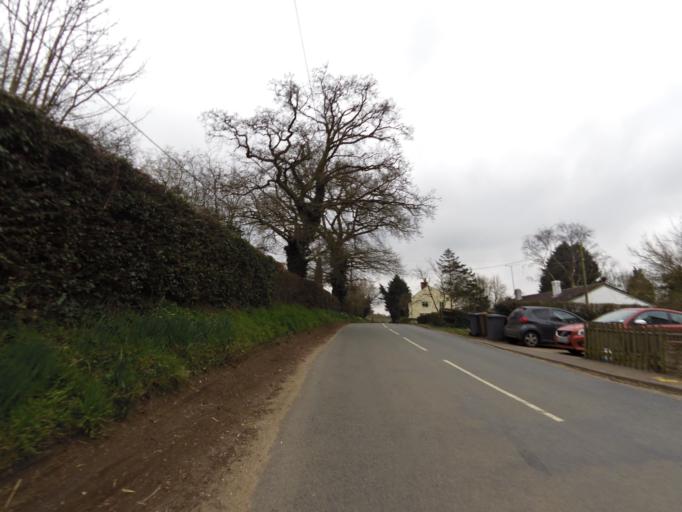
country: GB
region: England
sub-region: Suffolk
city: Wickham Market
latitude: 52.1772
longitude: 1.3418
